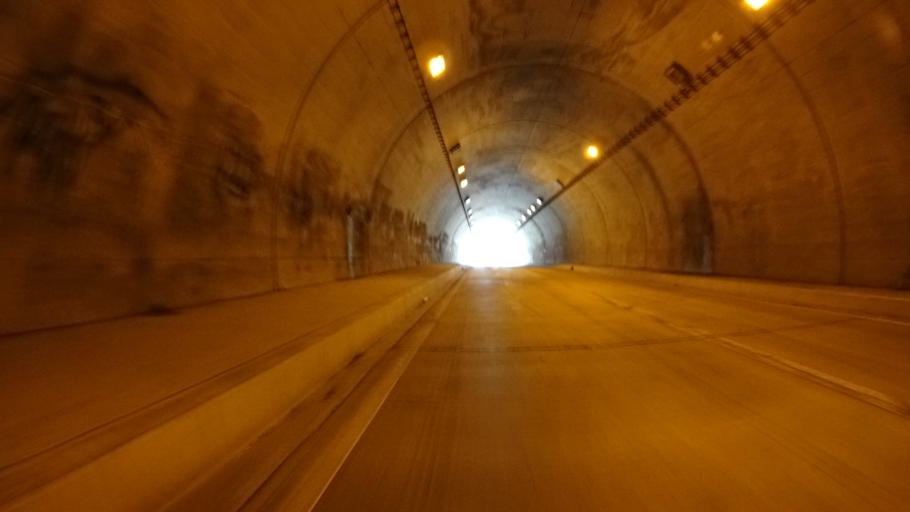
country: JP
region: Kanagawa
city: Hadano
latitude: 35.5119
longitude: 139.2314
